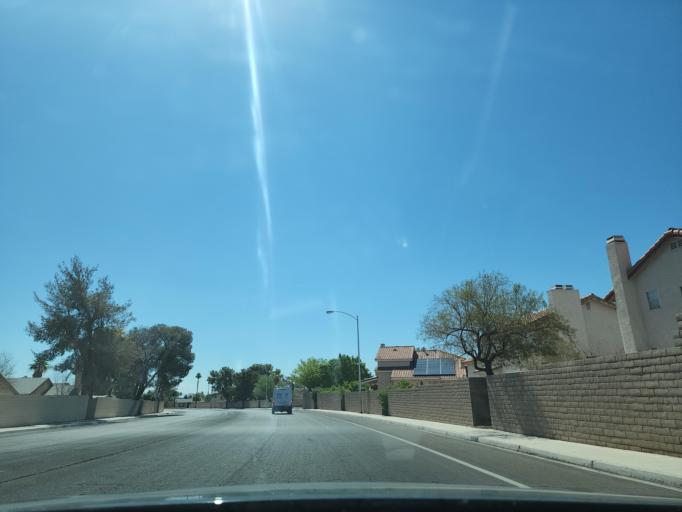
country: US
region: Nevada
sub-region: Clark County
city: Spring Valley
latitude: 36.1035
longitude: -115.2532
